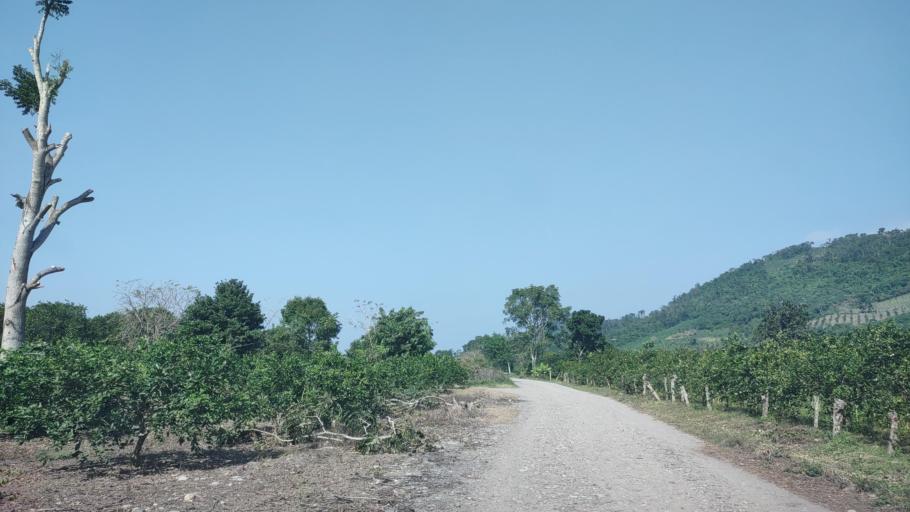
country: MX
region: Veracruz
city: Agua Dulce
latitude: 20.2792
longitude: -97.2857
